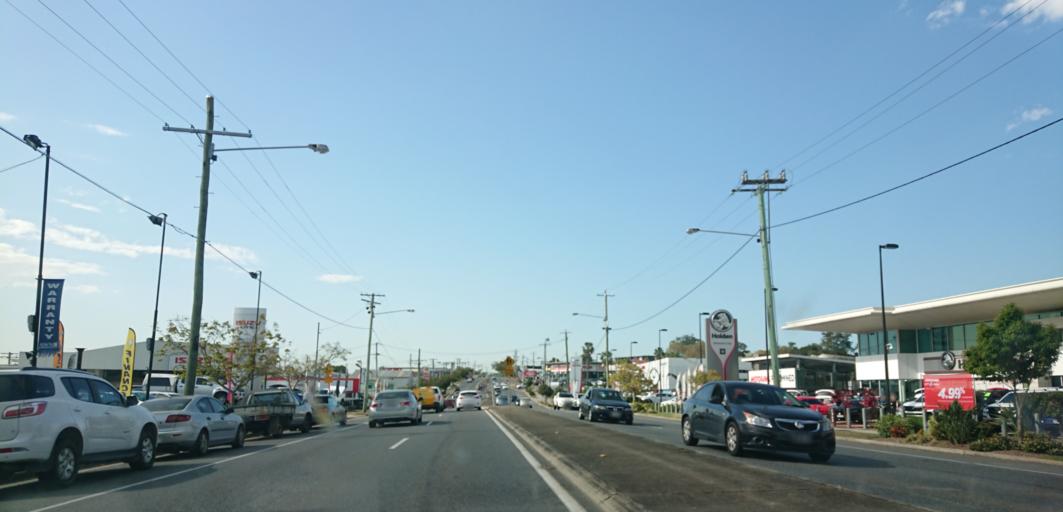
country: AU
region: Queensland
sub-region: Brisbane
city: Rocklea
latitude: -27.5340
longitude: 153.0155
